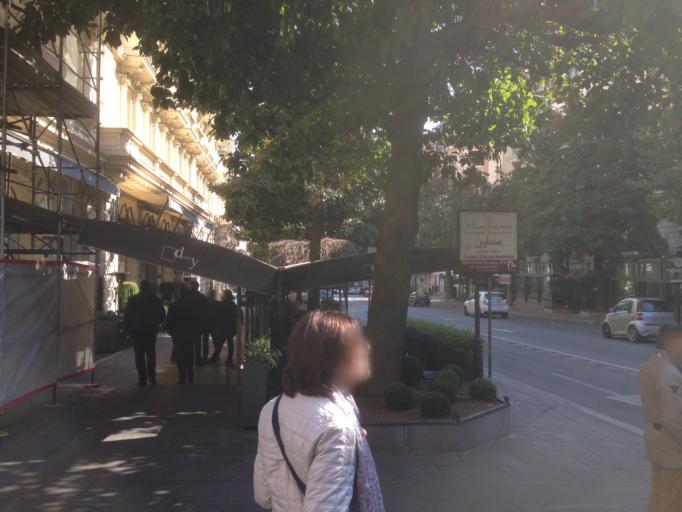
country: IT
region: Latium
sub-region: Citta metropolitana di Roma Capitale
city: Rome
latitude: 41.9082
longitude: 12.4894
